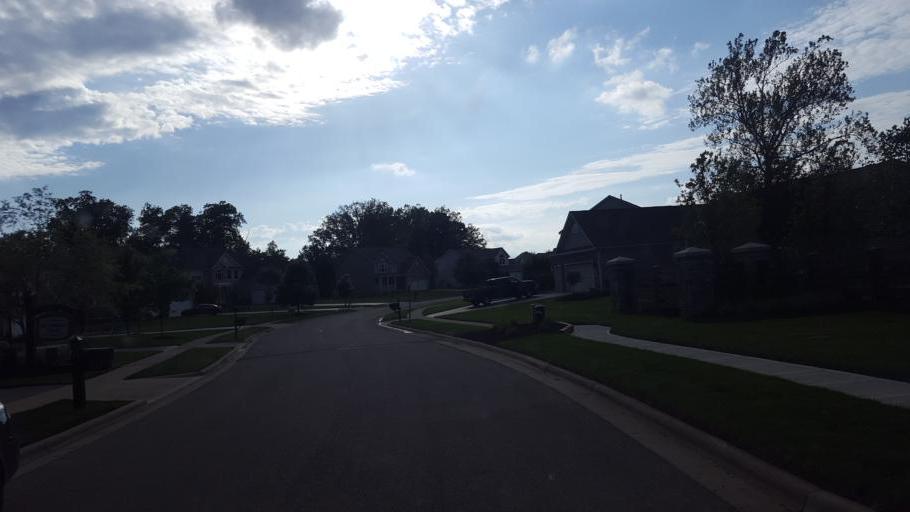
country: US
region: Ohio
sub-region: Delaware County
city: Lewis Center
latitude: 40.1776
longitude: -82.9756
